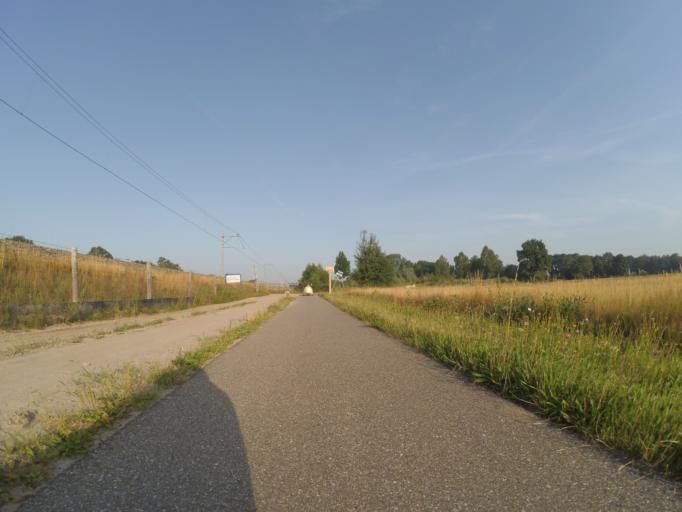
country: NL
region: Overijssel
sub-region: Gemeente Wierden
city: Wierden
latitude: 52.3640
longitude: 6.4991
